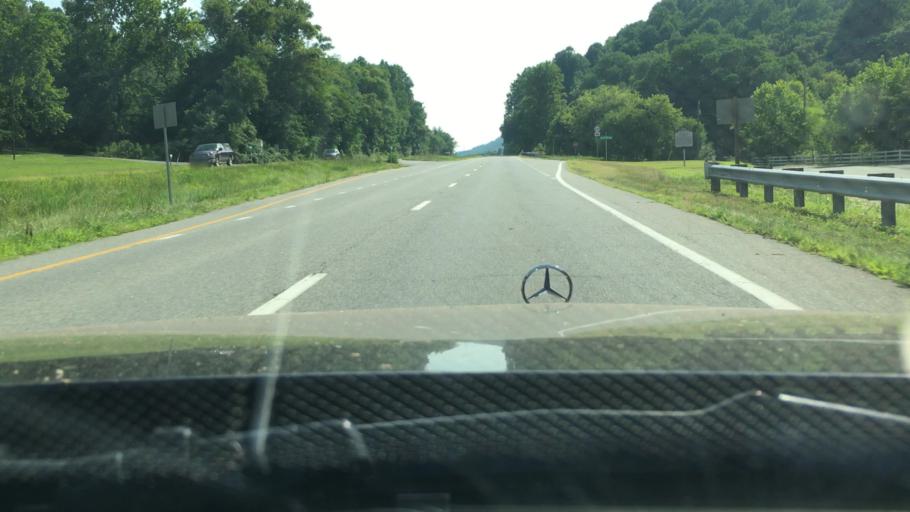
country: US
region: Virginia
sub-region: Nelson County
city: Nellysford
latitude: 37.8909
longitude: -78.7043
